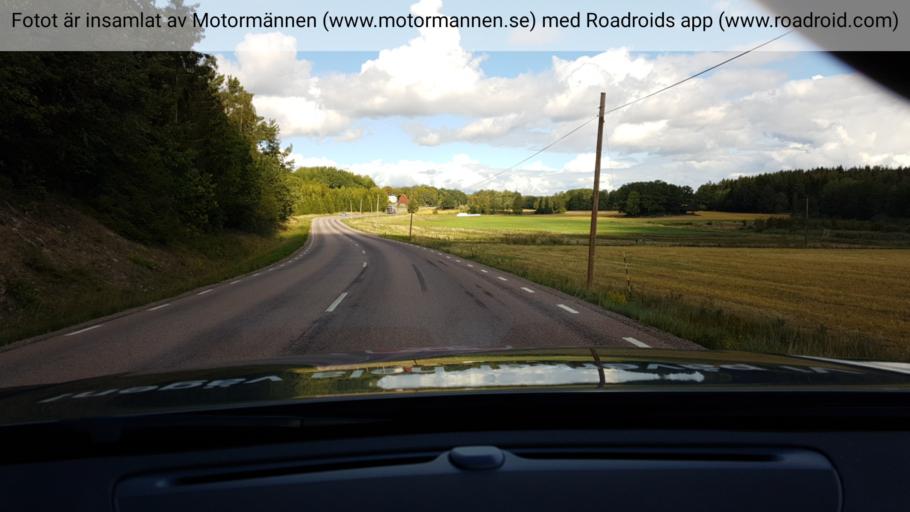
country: SE
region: Soedermanland
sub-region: Strangnas Kommun
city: Mariefred
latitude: 59.3036
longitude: 17.2191
